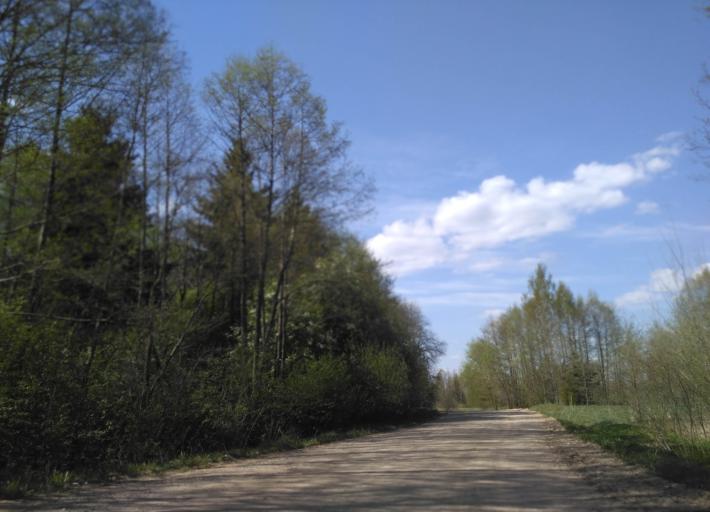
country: BY
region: Minsk
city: Narach
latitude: 54.9742
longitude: 26.6252
